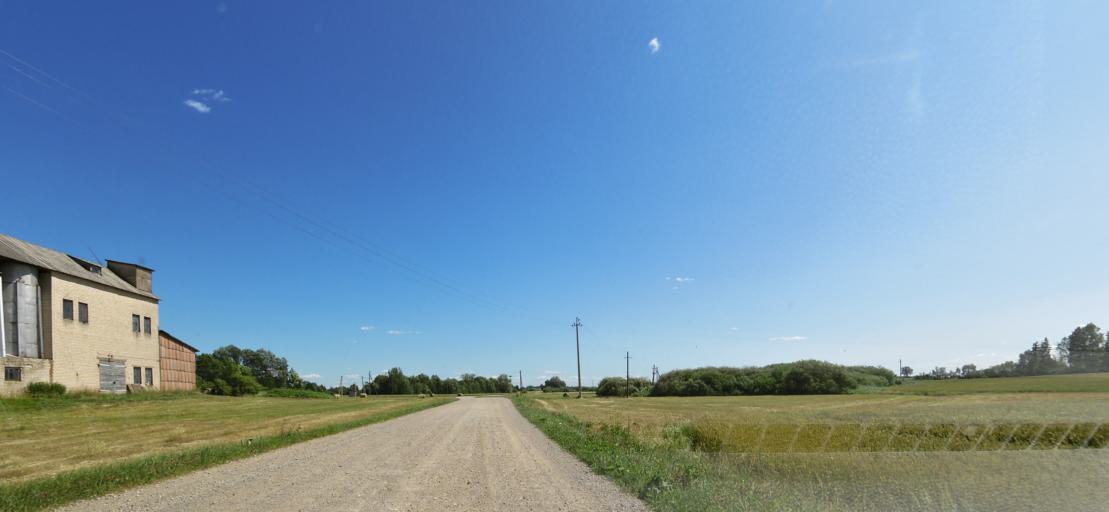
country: LV
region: Bauskas Rajons
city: Bauska
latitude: 56.2847
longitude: 24.3417
